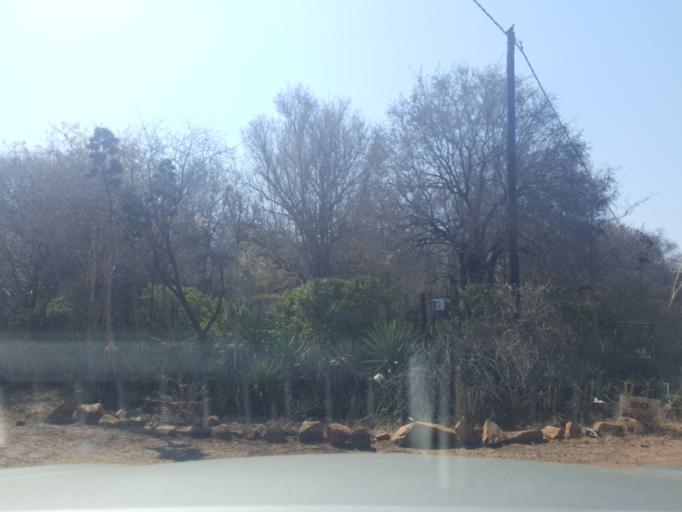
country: BW
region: Kweneng
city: Gabane
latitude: -24.7423
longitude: 25.8293
